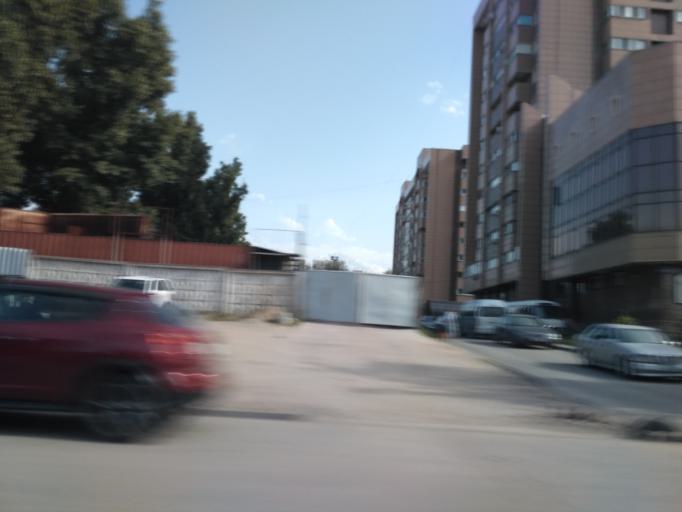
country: KZ
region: Almaty Qalasy
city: Almaty
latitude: 43.2451
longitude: 76.8538
